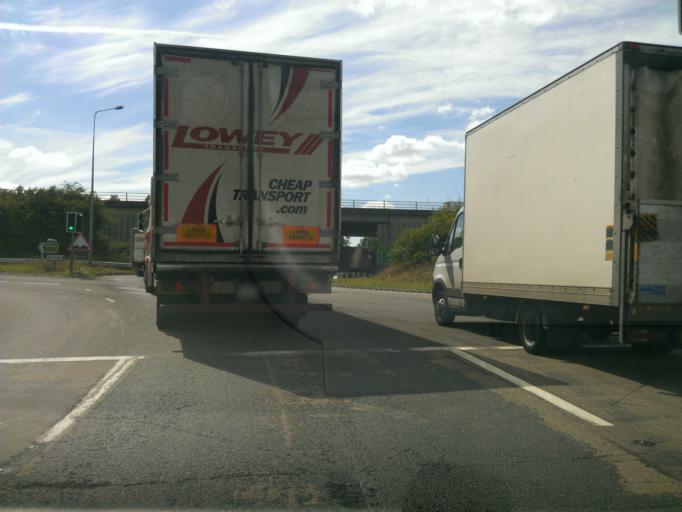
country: GB
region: England
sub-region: Cambridgeshire
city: Brampton
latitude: 52.3323
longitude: -0.2469
